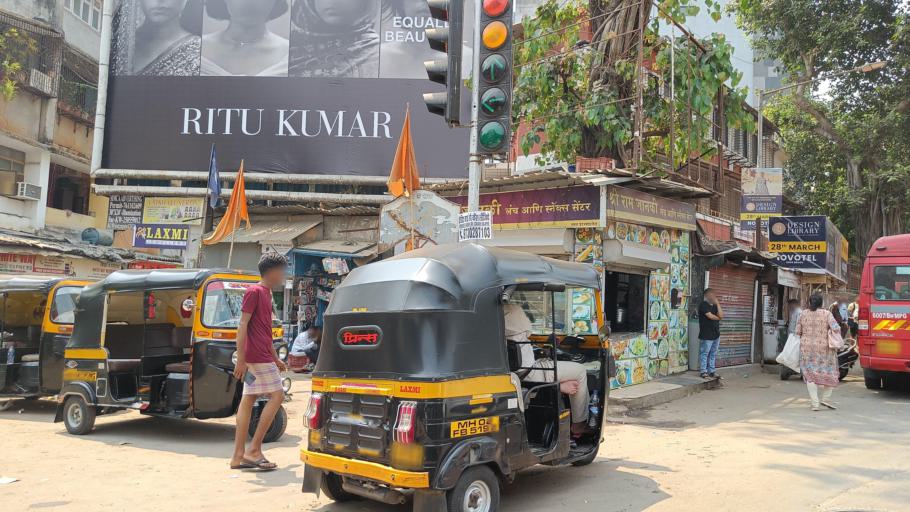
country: IN
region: Maharashtra
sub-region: Mumbai Suburban
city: Mumbai
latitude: 19.0922
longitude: 72.8282
